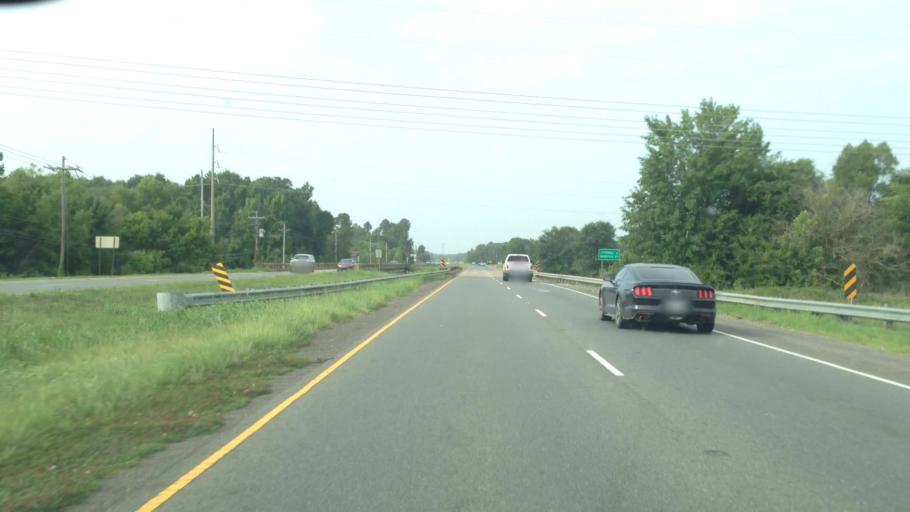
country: US
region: Louisiana
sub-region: De Soto Parish
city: Stonewall
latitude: 32.3779
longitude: -93.8210
